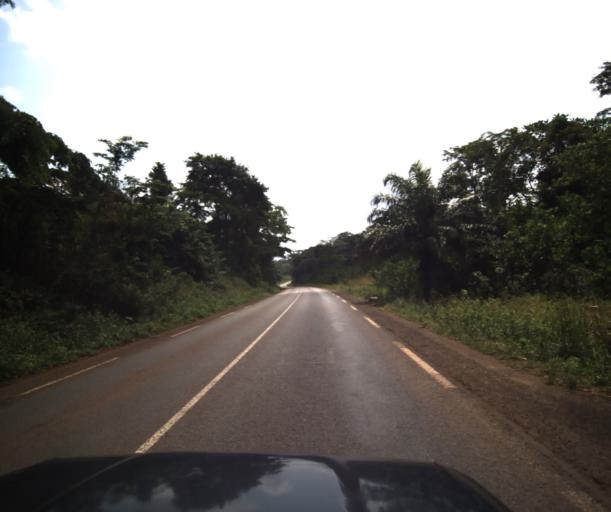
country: CM
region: Centre
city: Eseka
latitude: 3.8902
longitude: 10.7860
